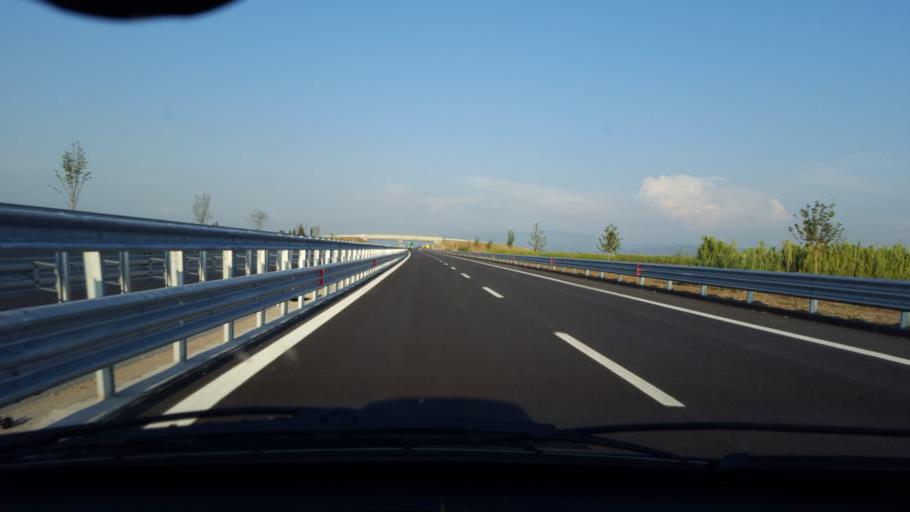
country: AL
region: Fier
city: Fier
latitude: 40.7483
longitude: 19.5356
